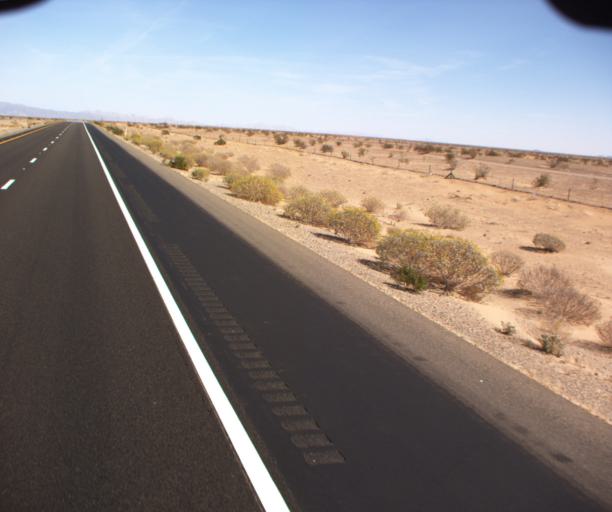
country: US
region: Arizona
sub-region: Yuma County
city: Somerton
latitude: 32.4951
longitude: -114.5840
